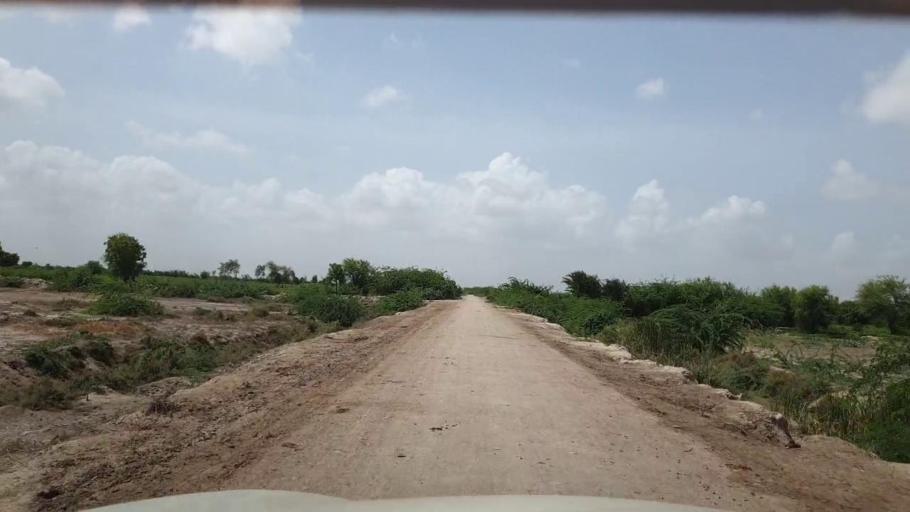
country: PK
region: Sindh
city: Kadhan
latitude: 24.4256
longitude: 68.8322
